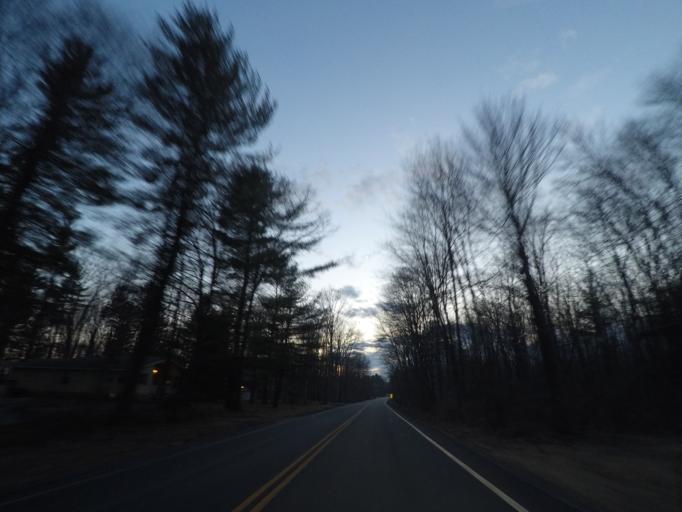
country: US
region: New York
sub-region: Schenectady County
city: Niskayuna
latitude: 42.8325
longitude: -73.8054
